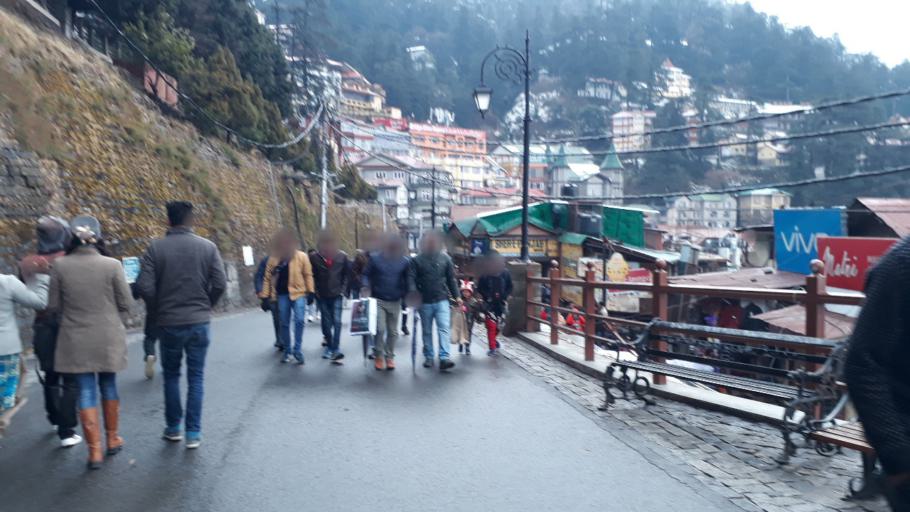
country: IN
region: Himachal Pradesh
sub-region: Shimla
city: Shimla
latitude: 31.1036
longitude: 77.1768
